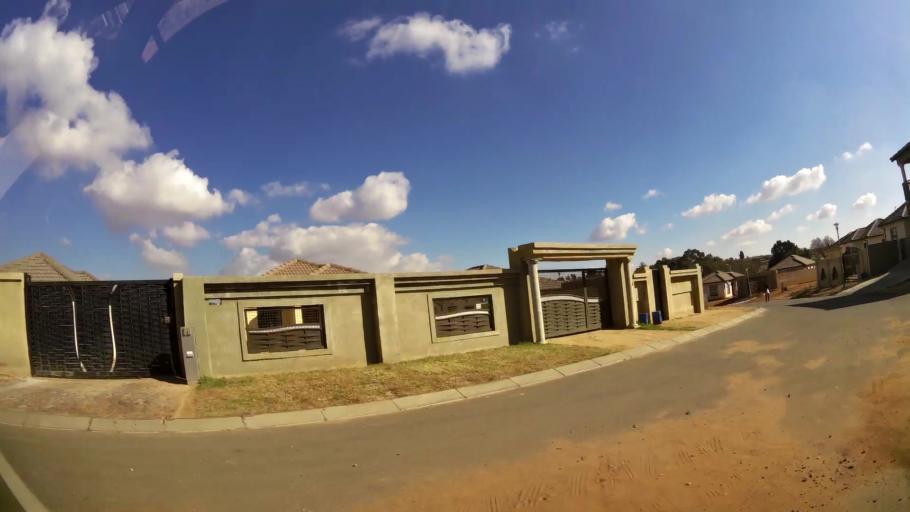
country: ZA
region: Gauteng
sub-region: City of Johannesburg Metropolitan Municipality
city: Roodepoort
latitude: -26.1401
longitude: 27.8235
